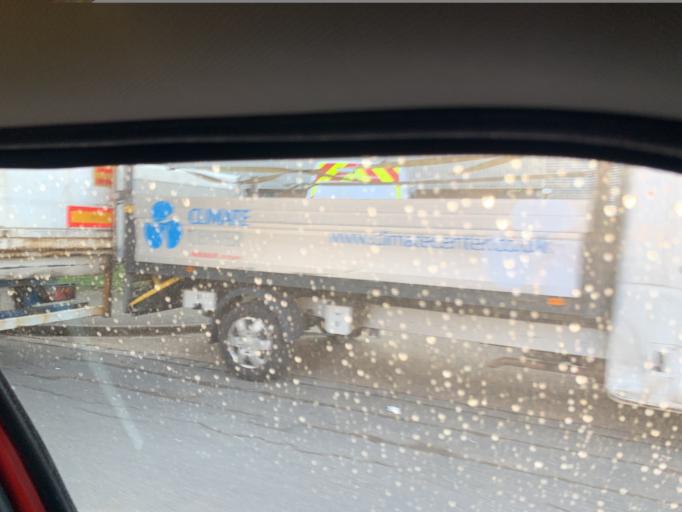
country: GB
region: England
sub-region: Buckinghamshire
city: Farnham Royal
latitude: 51.5187
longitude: -0.6175
